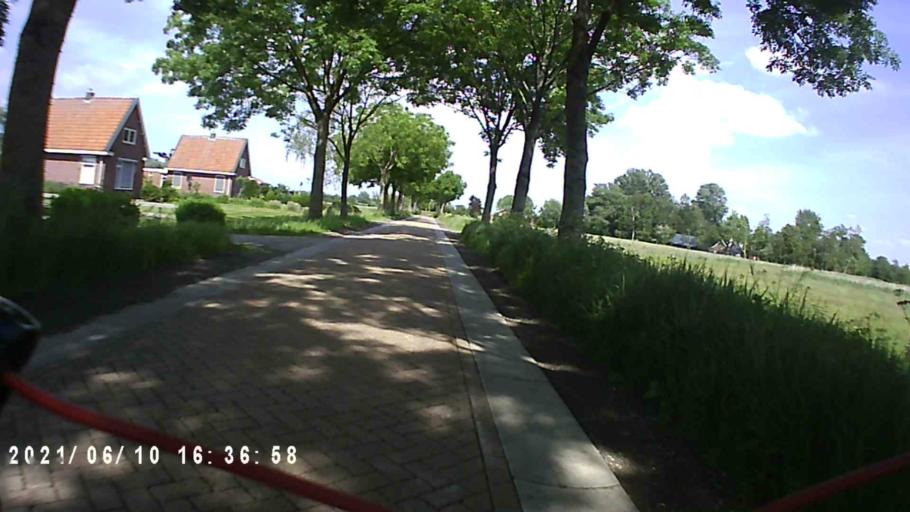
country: NL
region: Friesland
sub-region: Gemeente Achtkarspelen
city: Buitenpost
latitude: 53.2389
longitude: 6.1409
